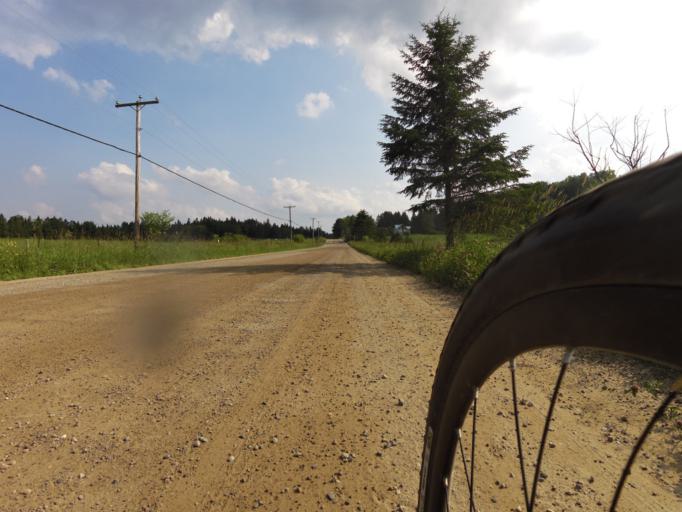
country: CA
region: Quebec
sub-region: Laurentides
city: Mont-Tremblant
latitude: 45.9547
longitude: -74.5933
